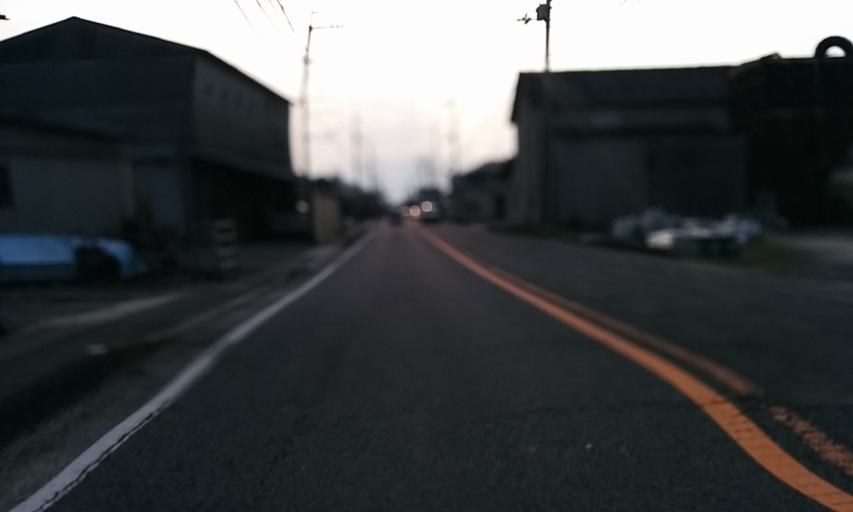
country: JP
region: Ehime
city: Saijo
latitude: 33.8949
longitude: 133.1490
